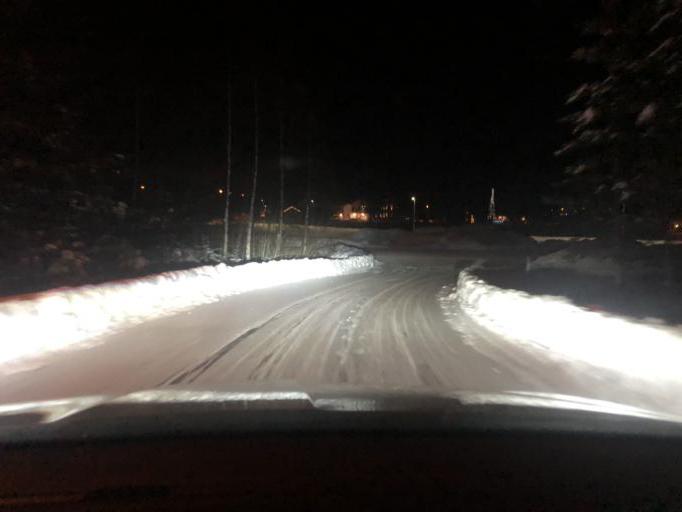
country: SE
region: Vaesterbotten
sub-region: Skelleftea Kommun
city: Byske
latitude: 65.0316
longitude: 21.3320
